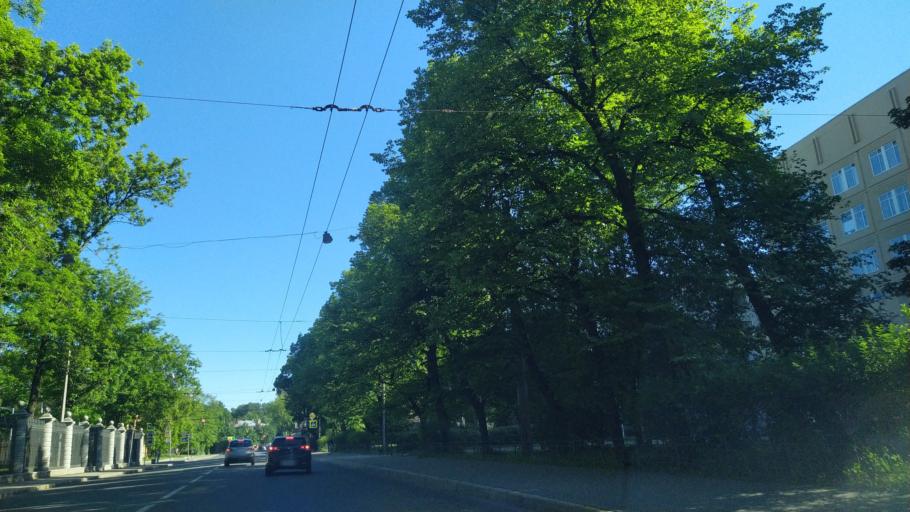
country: RU
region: Leningrad
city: Finlyandskiy
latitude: 59.9628
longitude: 30.3443
